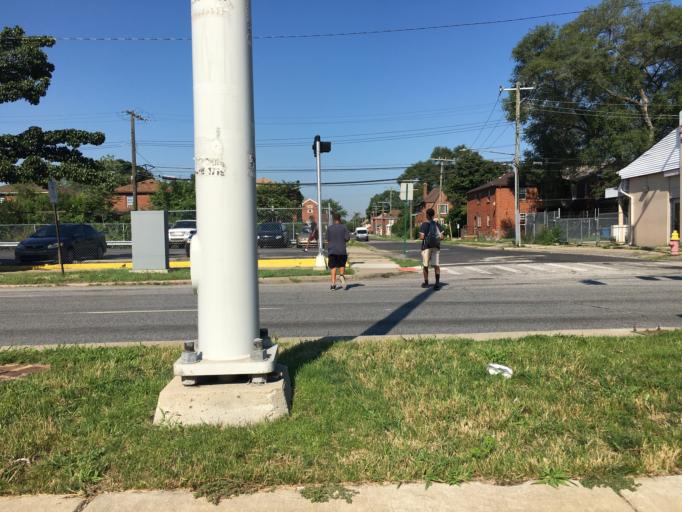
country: US
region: Michigan
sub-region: Oakland County
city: Ferndale
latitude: 42.4189
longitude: -83.1409
